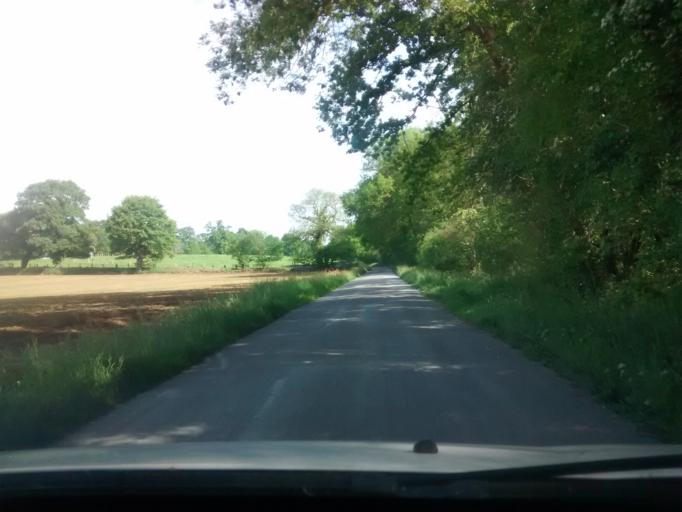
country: FR
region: Brittany
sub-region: Departement d'Ille-et-Vilaine
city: Javene
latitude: 48.3355
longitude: -1.2157
